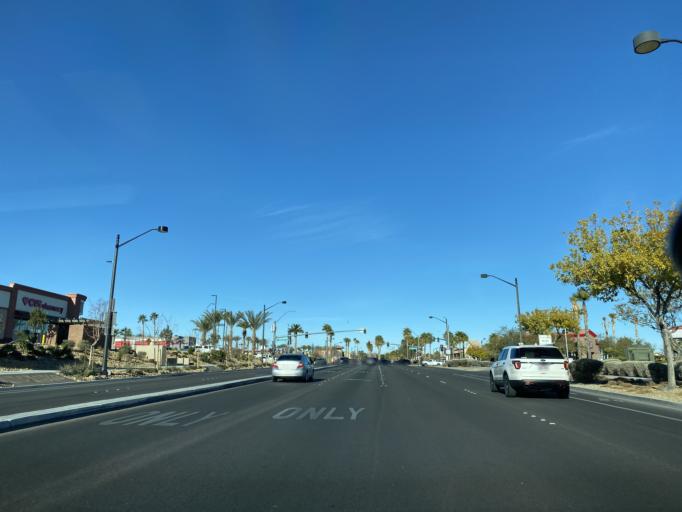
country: US
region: Nevada
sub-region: Clark County
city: Summerlin South
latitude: 36.3003
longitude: -115.2815
